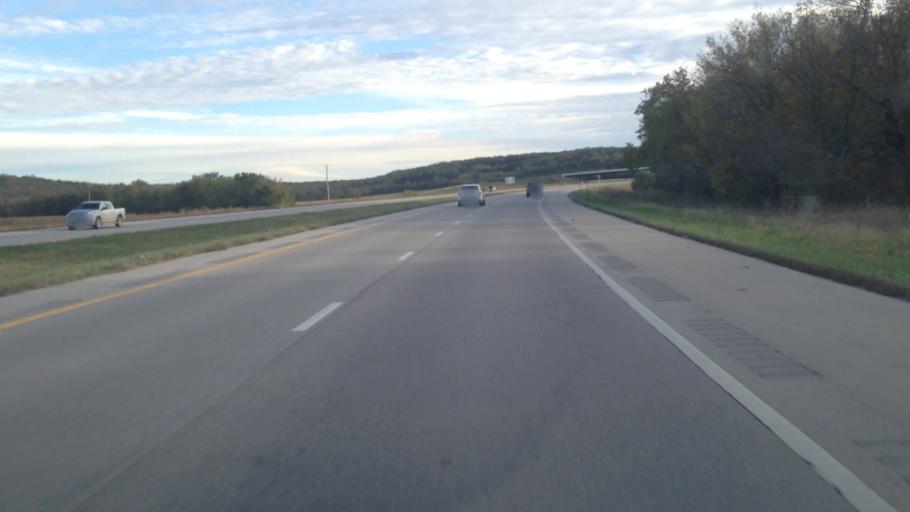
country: US
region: Kansas
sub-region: Douglas County
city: Lawrence
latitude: 38.8754
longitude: -95.2561
